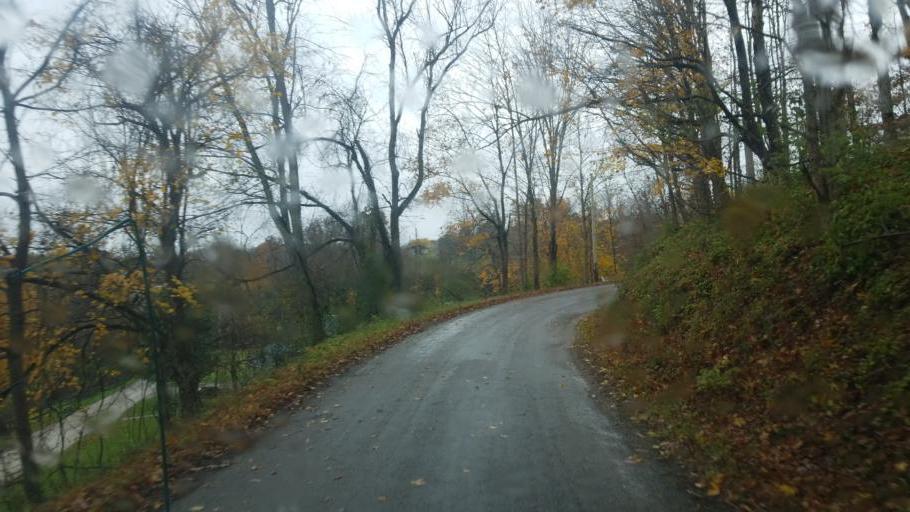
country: US
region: Ohio
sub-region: Washington County
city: Belpre
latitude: 39.3151
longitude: -81.6036
